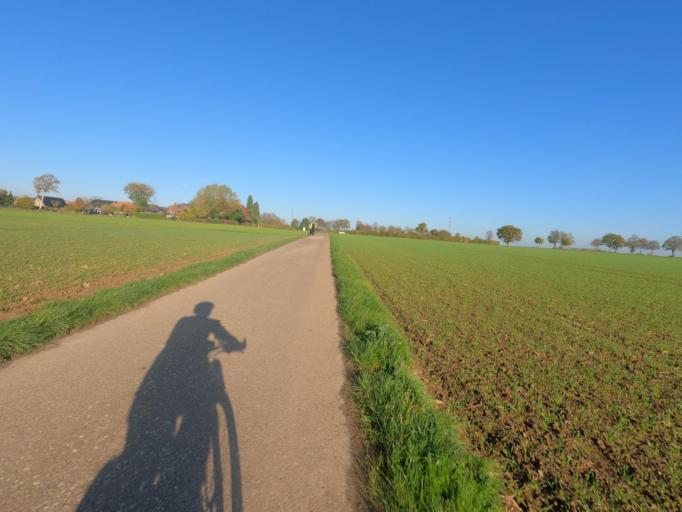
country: DE
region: North Rhine-Westphalia
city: Erkelenz
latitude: 51.0805
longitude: 6.3502
